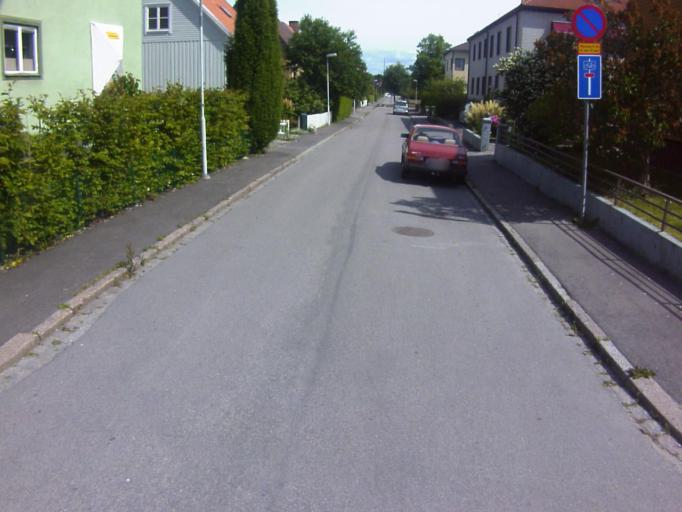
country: SE
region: Soedermanland
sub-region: Eskilstuna Kommun
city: Eskilstuna
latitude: 59.3604
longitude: 16.5238
